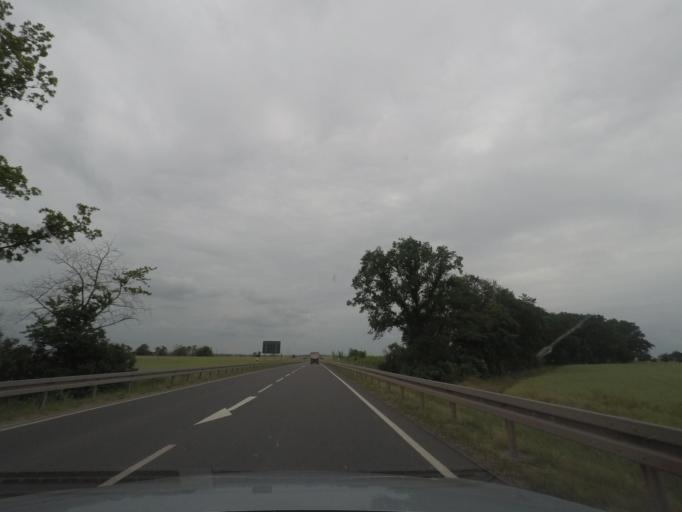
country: DE
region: Saxony-Anhalt
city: Suplingen
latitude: 52.2469
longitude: 11.3260
